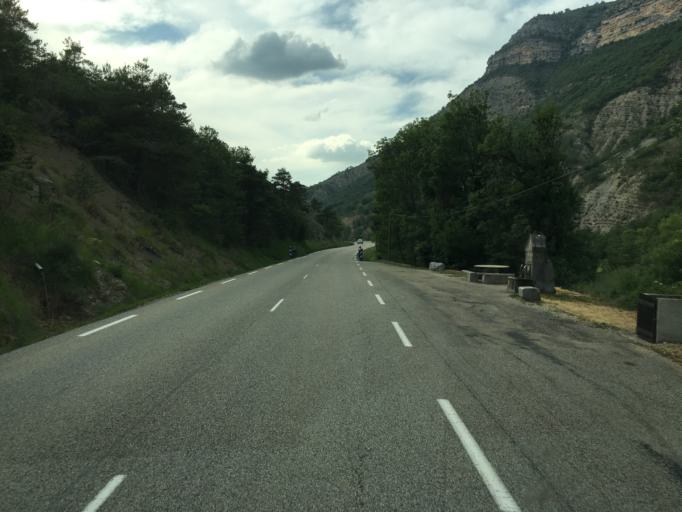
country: FR
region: Rhone-Alpes
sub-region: Departement de la Drome
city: Buis-les-Baronnies
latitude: 44.3902
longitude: 5.3700
